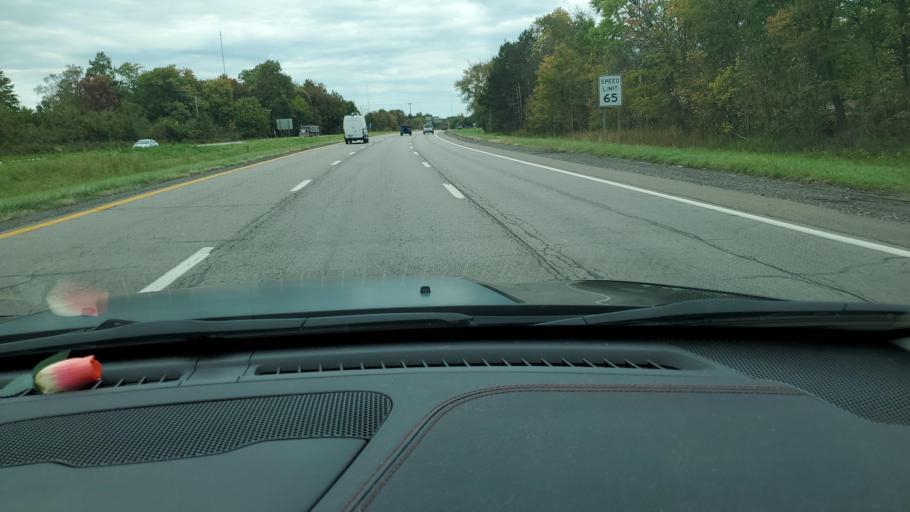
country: US
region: Ohio
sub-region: Mahoning County
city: Poland
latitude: 41.0336
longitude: -80.6306
